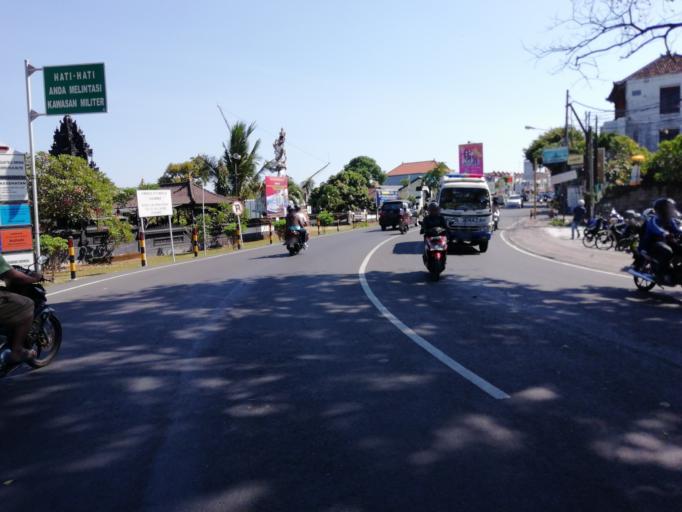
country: ID
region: Bali
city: Karyadharma
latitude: -8.7107
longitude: 115.2213
